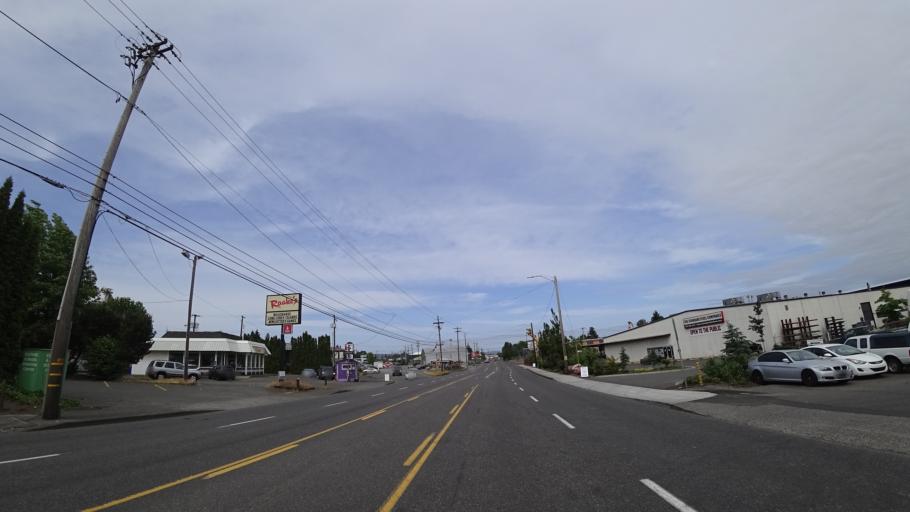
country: US
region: Oregon
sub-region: Multnomah County
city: Portland
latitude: 45.5771
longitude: -122.6464
